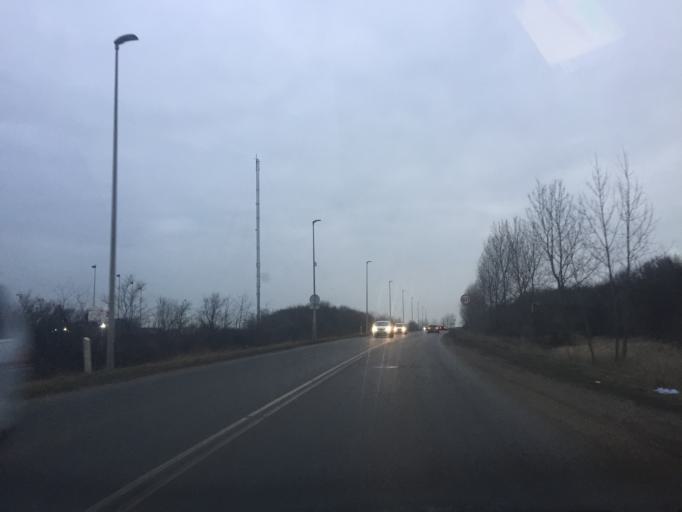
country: DK
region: Zealand
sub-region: Koge Kommune
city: Koge
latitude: 55.4716
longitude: 12.1898
